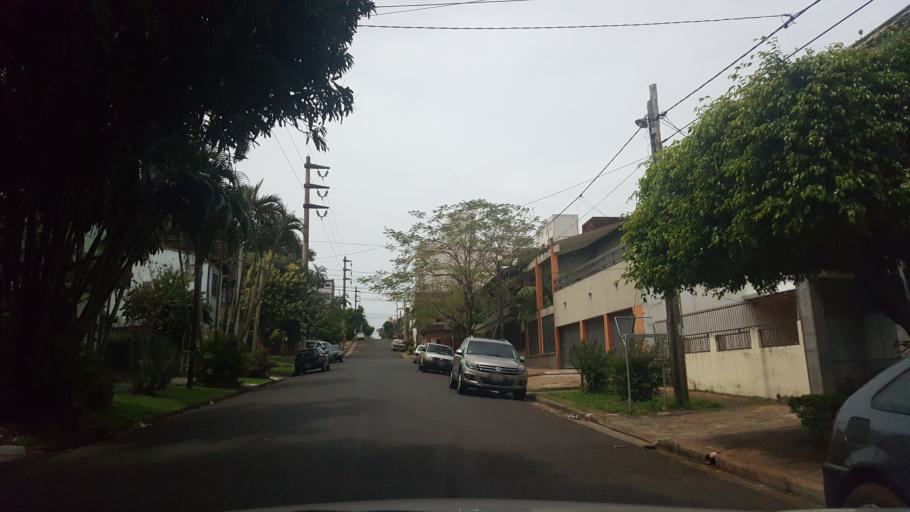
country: AR
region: Misiones
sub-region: Departamento de Capital
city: Posadas
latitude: -27.3583
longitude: -55.9009
